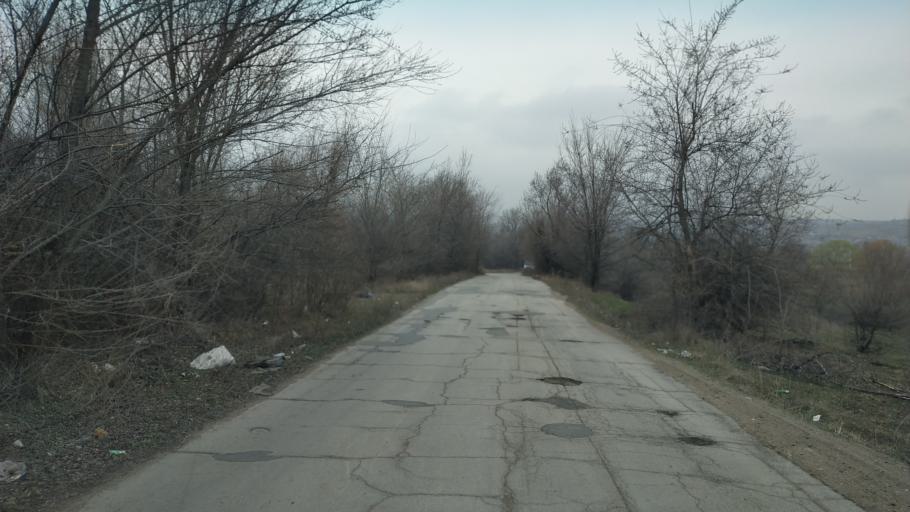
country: MD
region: Chisinau
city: Singera
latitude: 46.9228
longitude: 29.0046
